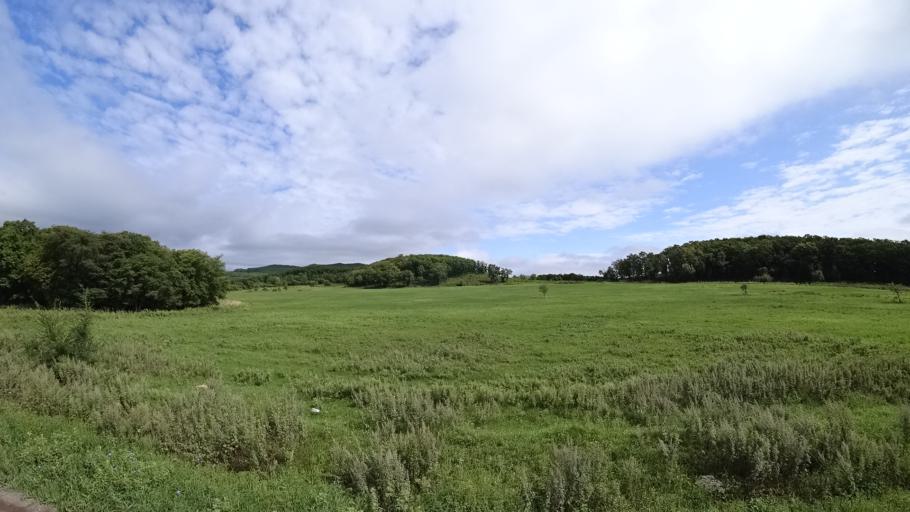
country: RU
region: Primorskiy
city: Lyalichi
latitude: 44.1432
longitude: 132.3891
